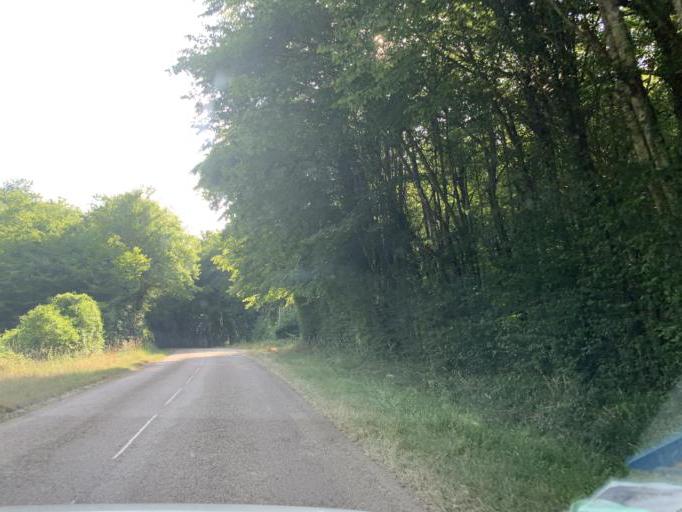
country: FR
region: Bourgogne
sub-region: Departement de l'Yonne
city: Fontenailles
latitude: 47.5179
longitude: 3.4064
